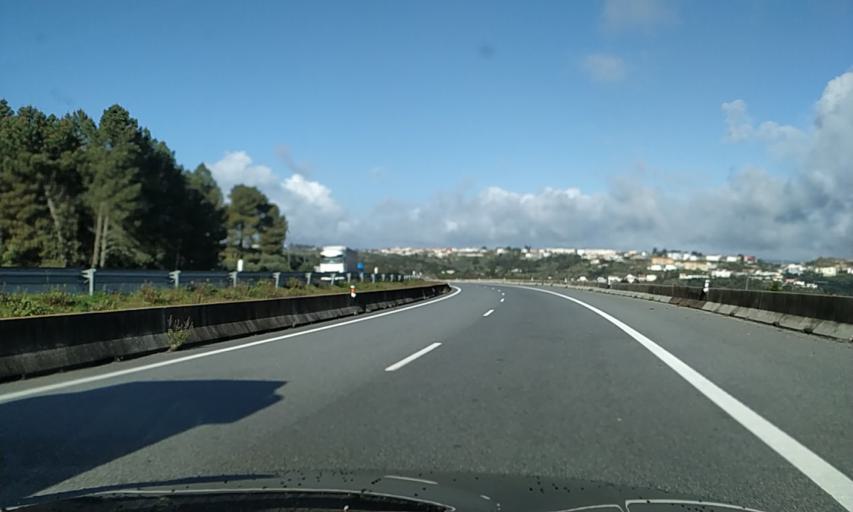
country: PT
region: Guarda
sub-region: Celorico da Beira
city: Celorico da Beira
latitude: 40.6279
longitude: -7.3719
